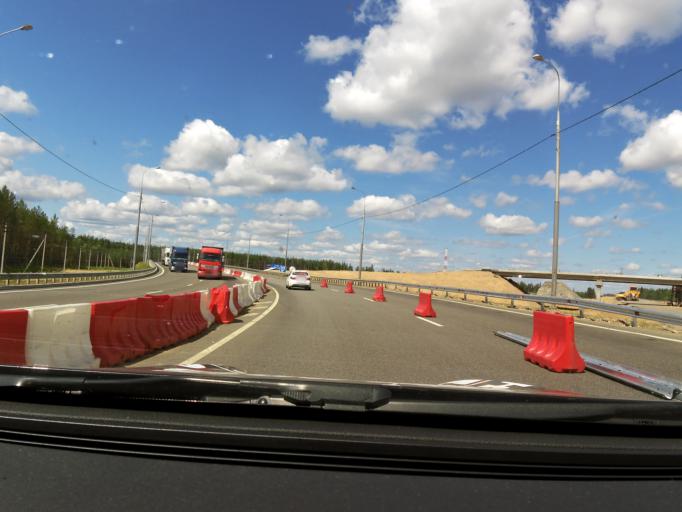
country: RU
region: Tverskaya
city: Bologoye
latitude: 57.7007
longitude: 34.2041
